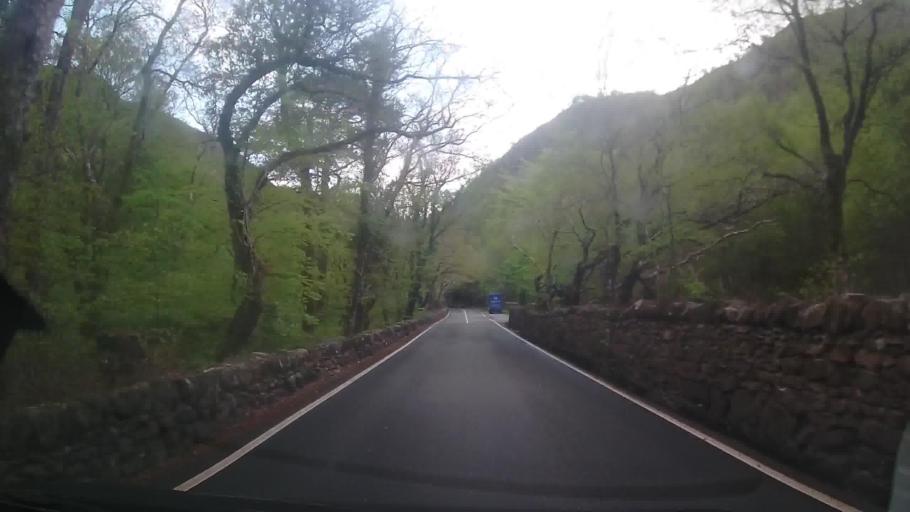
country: GB
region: Wales
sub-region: Gwynedd
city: Penrhyndeudraeth
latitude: 53.0022
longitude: -4.0973
